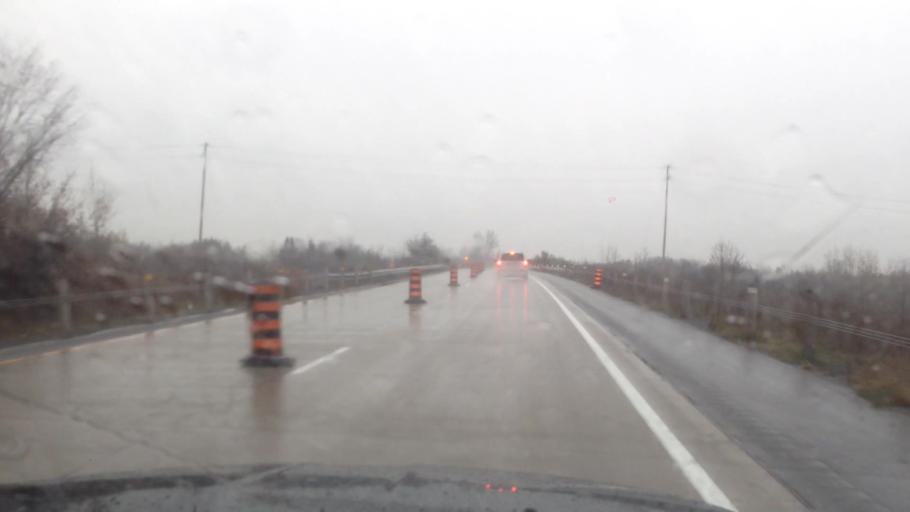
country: CA
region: Ontario
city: Hawkesbury
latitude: 45.4821
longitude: -74.6401
